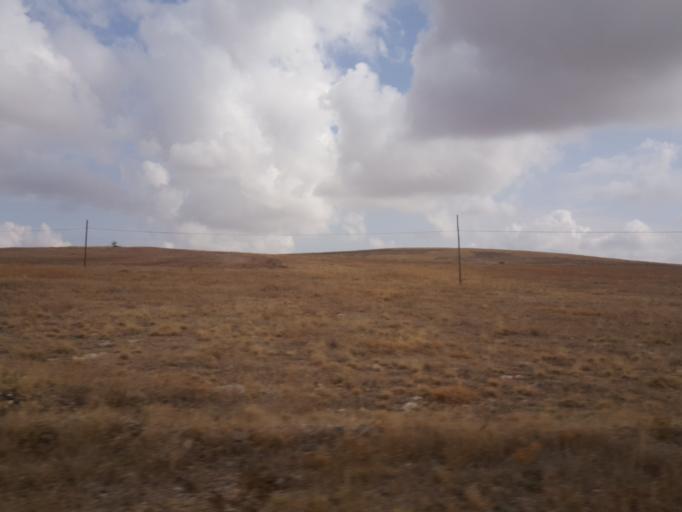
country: TR
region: Kirikkale
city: Keskin
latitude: 39.6372
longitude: 33.6078
